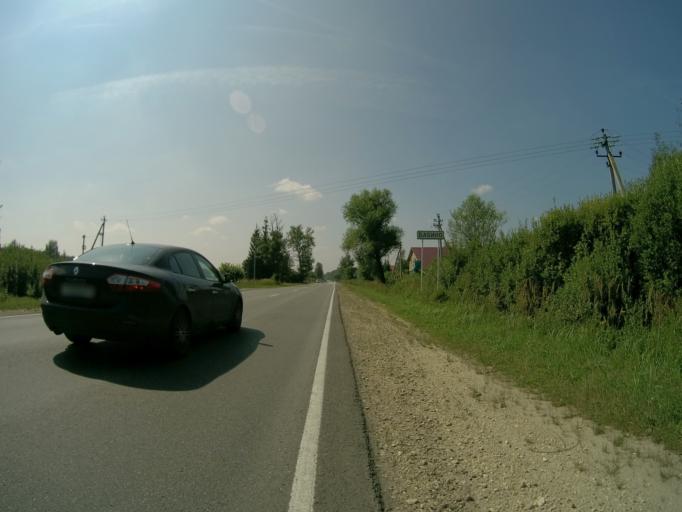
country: RU
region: Vladimir
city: Anopino
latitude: 55.6909
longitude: 40.7470
